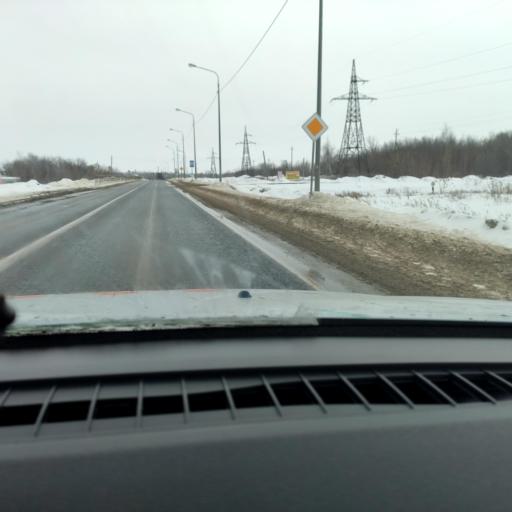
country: RU
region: Samara
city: Dubovyy Umet
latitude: 52.9717
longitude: 50.2773
